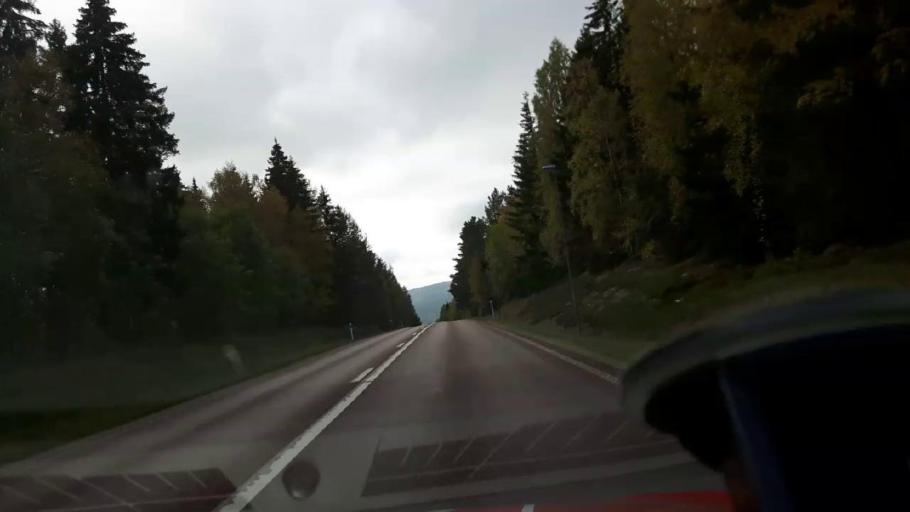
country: SE
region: Gaevleborg
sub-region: Ljusdals Kommun
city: Jaervsoe
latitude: 61.6864
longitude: 16.1477
